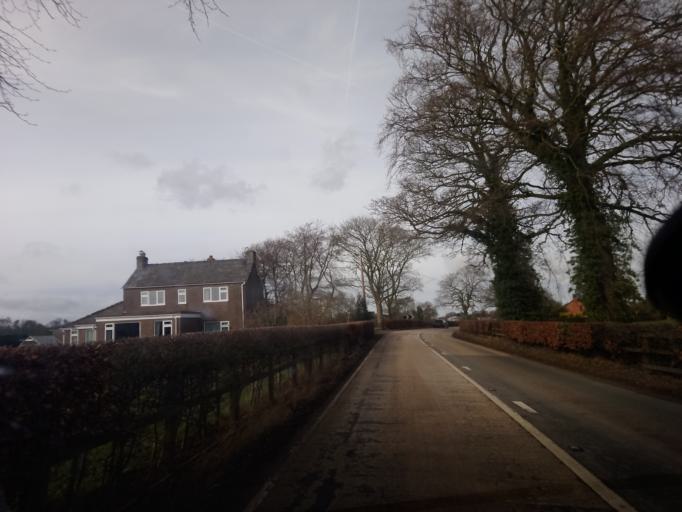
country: GB
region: England
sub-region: Shropshire
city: Prees
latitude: 52.8844
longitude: -2.6303
